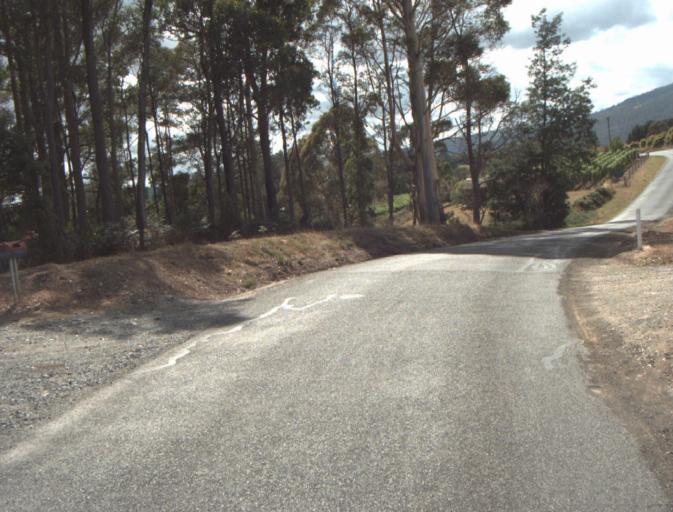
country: AU
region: Tasmania
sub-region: Launceston
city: Mayfield
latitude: -41.2581
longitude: 147.1898
